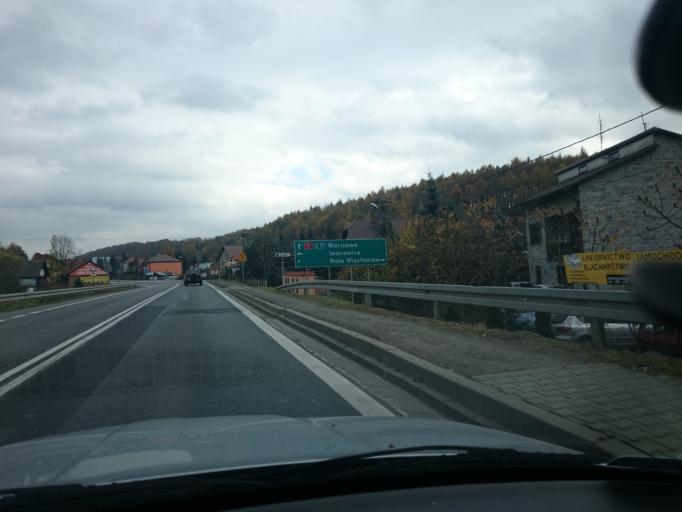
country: PL
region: Lesser Poland Voivodeship
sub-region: Powiat krakowski
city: Michalowice
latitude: 50.1735
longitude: 19.9821
